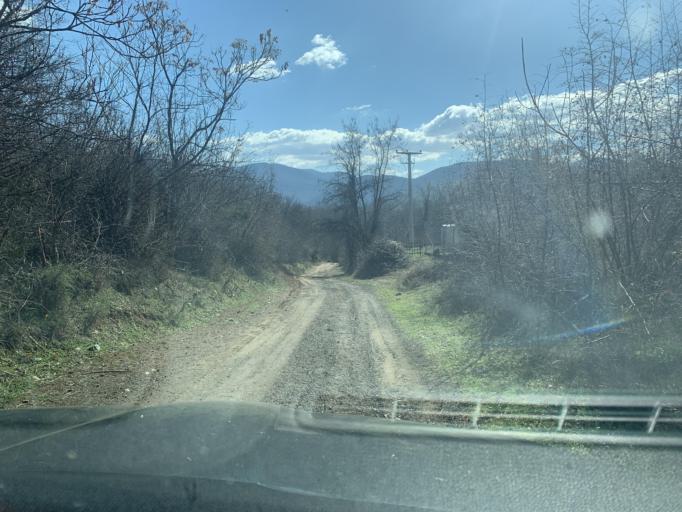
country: MK
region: Demir Kapija
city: Demir Kapija
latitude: 41.3985
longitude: 22.2179
